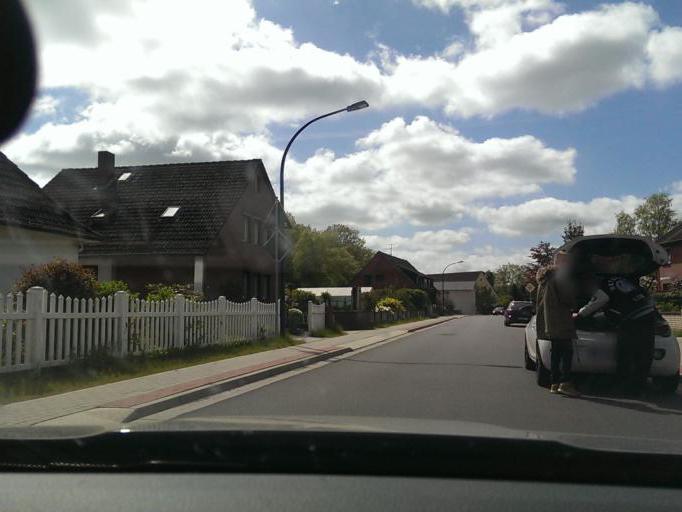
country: DE
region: Lower Saxony
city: Oyten
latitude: 53.0573
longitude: 9.0202
